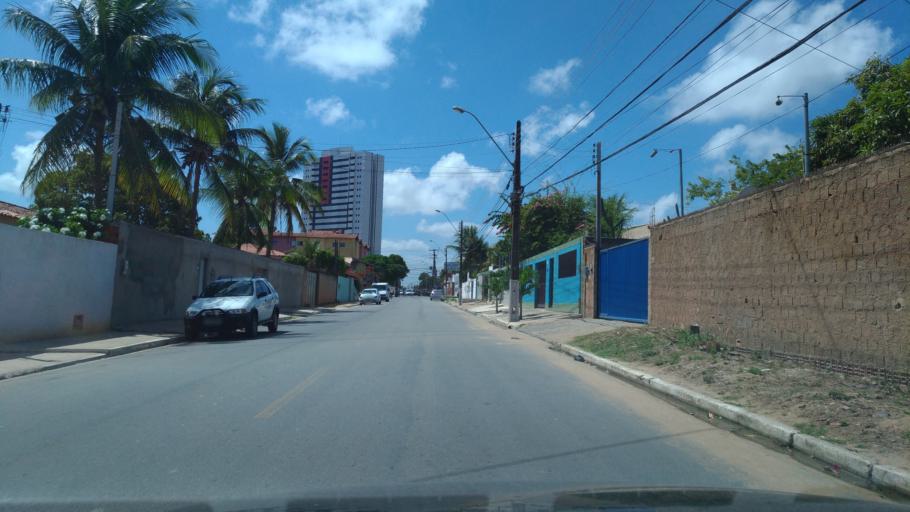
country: BR
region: Alagoas
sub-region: Maceio
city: Maceio
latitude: -9.6214
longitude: -35.7085
